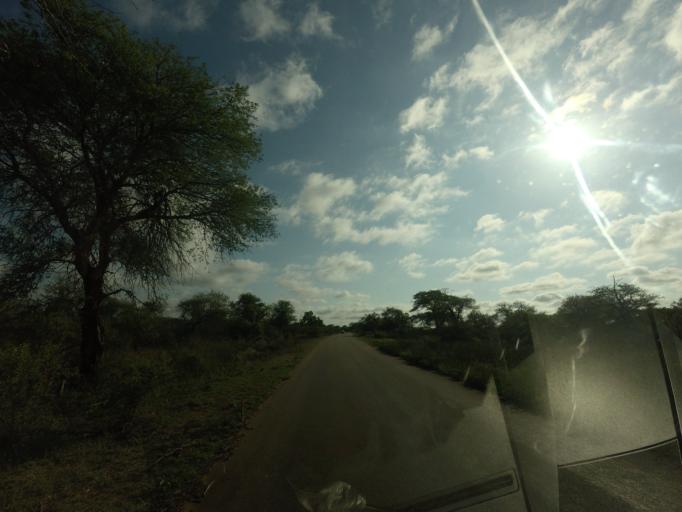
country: ZA
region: Mpumalanga
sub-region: Ehlanzeni District
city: Komatipoort
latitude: -25.2276
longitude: 31.8551
